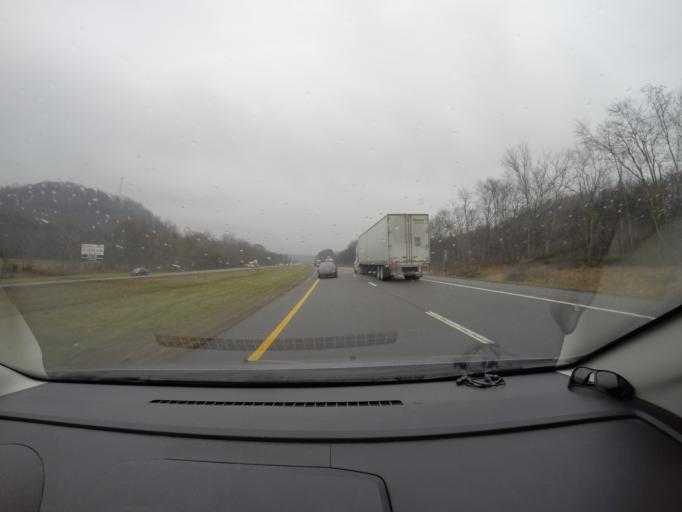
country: US
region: Tennessee
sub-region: Coffee County
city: New Union
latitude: 35.5682
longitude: -86.2265
